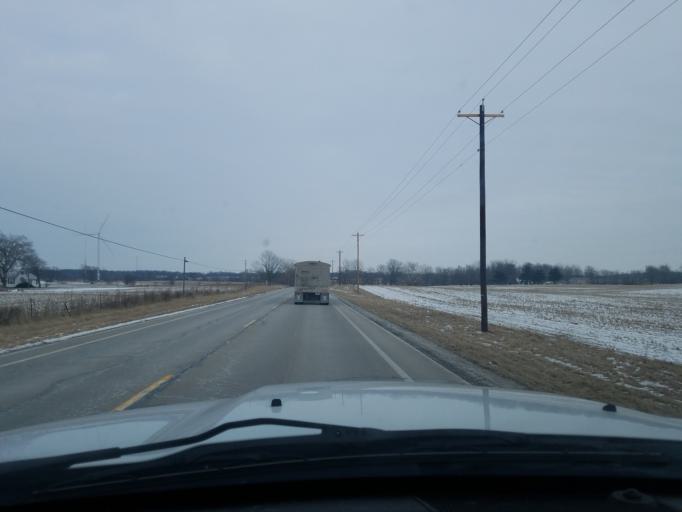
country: US
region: Indiana
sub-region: Randolph County
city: Lynn
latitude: 40.0485
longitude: -84.9743
